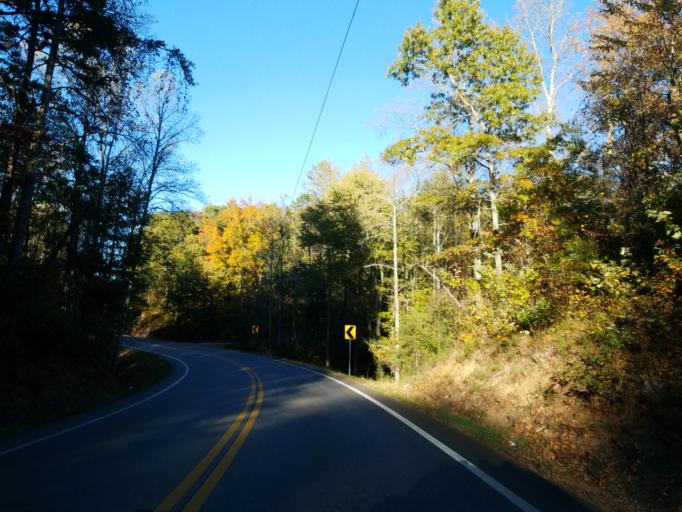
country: US
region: Georgia
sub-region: Dawson County
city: Dawsonville
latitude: 34.4269
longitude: -84.2210
